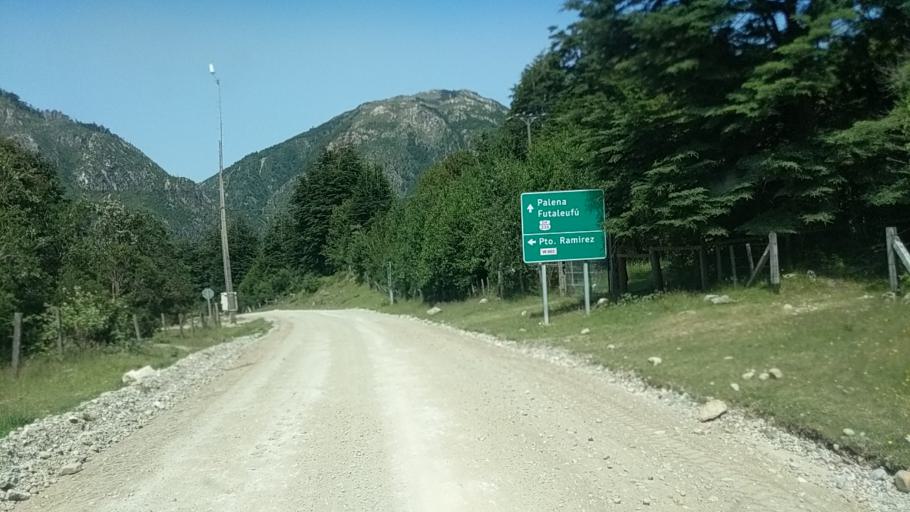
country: CL
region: Los Lagos
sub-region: Provincia de Palena
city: Palena
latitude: -43.4796
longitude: -72.1314
